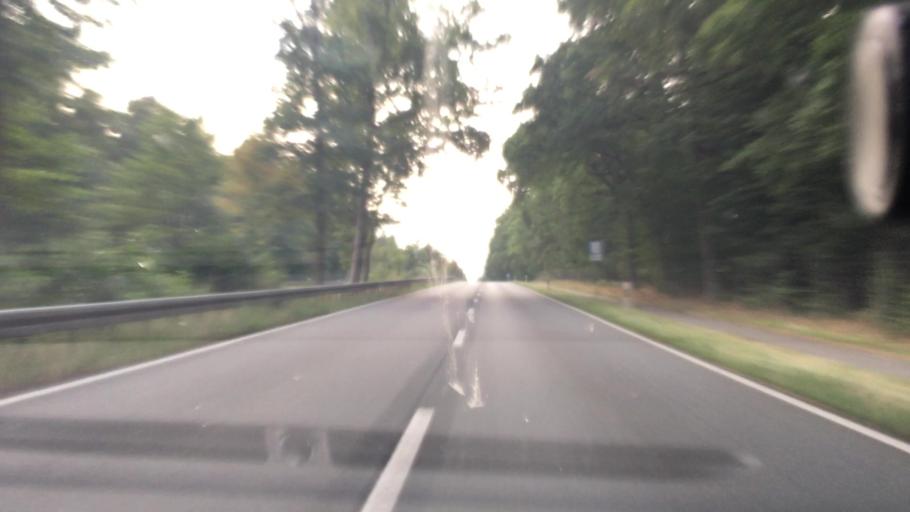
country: DE
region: Lower Saxony
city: Linsburg
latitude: 52.5591
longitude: 9.3337
